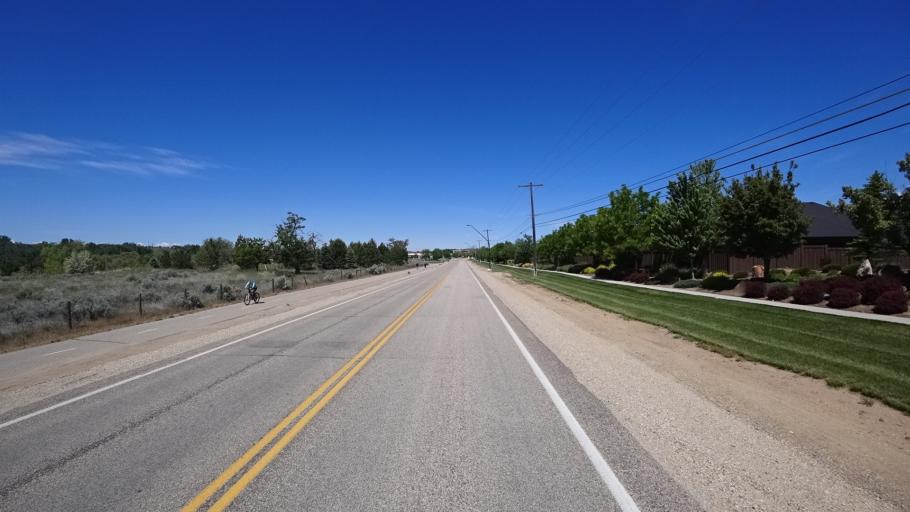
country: US
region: Idaho
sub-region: Ada County
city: Boise
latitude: 43.5632
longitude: -116.1085
